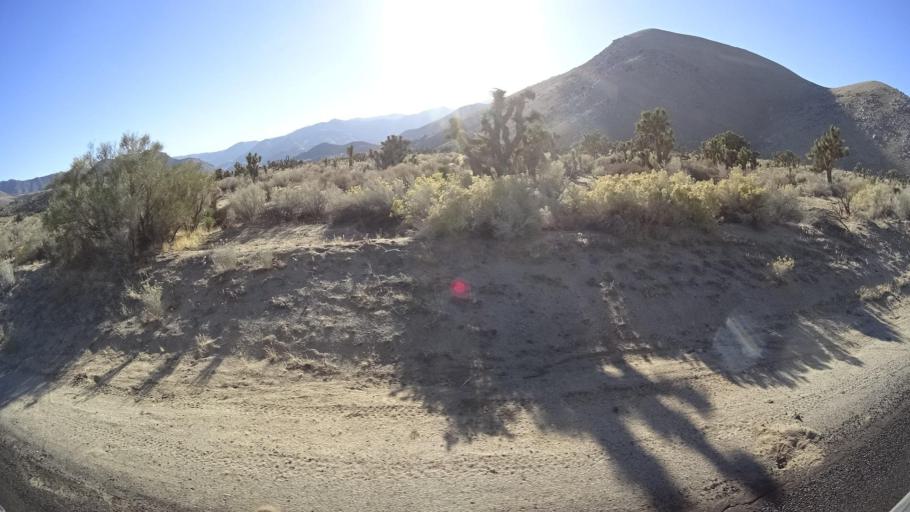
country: US
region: California
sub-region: Kern County
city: Weldon
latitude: 35.6117
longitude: -118.2440
